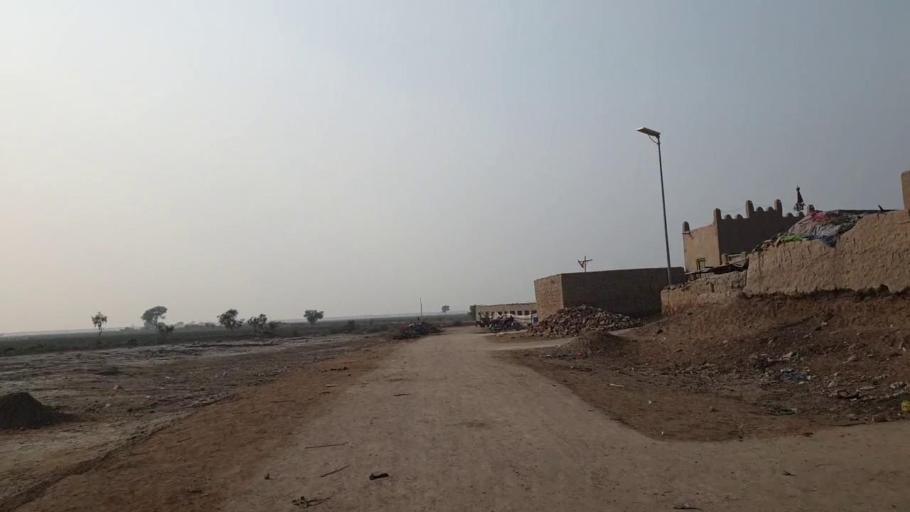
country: PK
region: Sindh
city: Bhan
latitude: 26.4705
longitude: 67.7040
